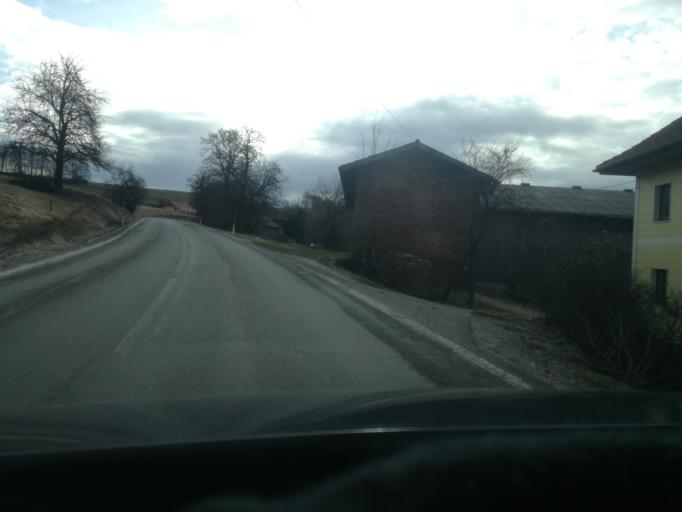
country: AT
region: Upper Austria
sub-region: Politischer Bezirk Vocklabruck
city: Frankenburg
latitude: 48.0812
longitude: 13.4850
